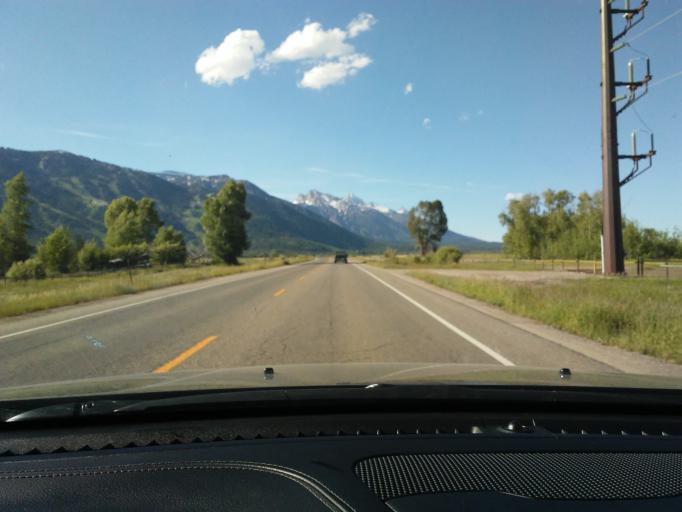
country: US
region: Wyoming
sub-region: Teton County
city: Moose Wilson Road
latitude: 43.5584
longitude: -110.8222
